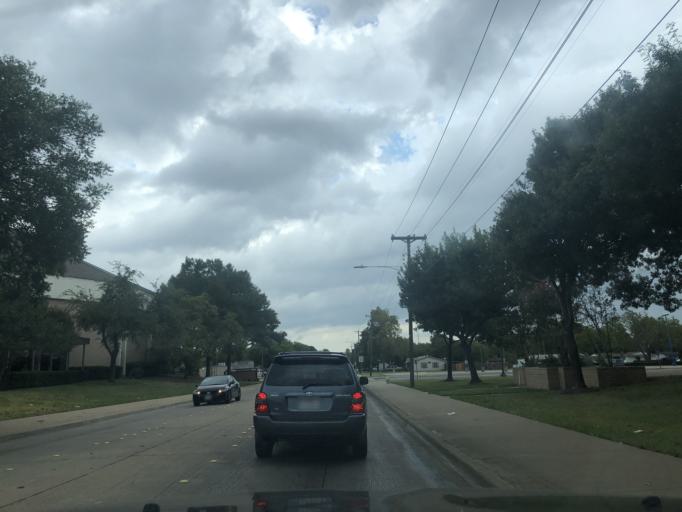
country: US
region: Texas
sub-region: Dallas County
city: Garland
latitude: 32.8799
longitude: -96.6480
